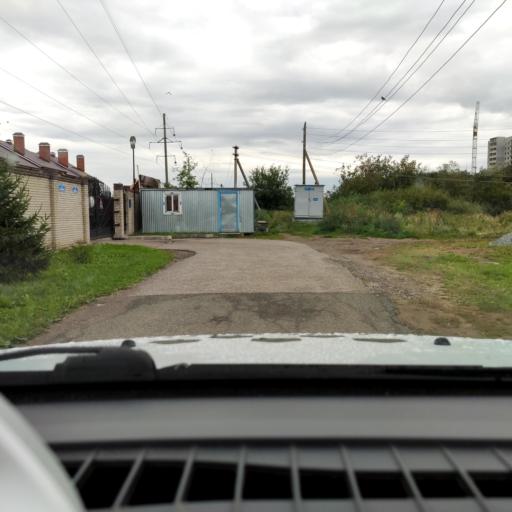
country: RU
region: Perm
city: Kondratovo
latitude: 57.9917
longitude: 56.1213
